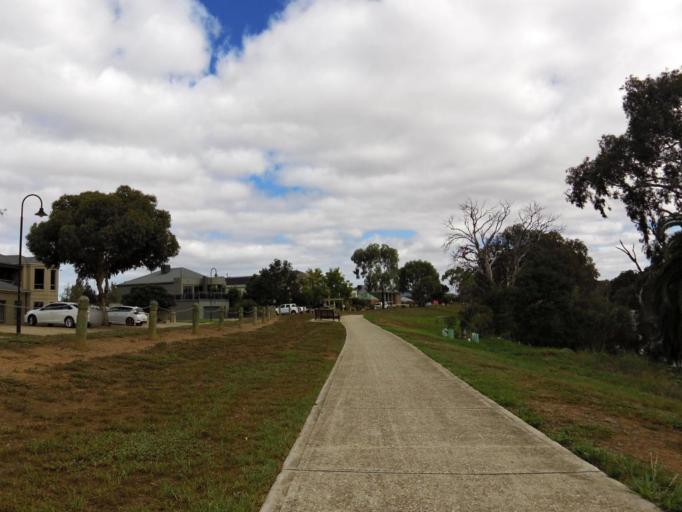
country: AU
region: Victoria
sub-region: Wyndham
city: Tarneit
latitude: -37.8771
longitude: 144.6526
